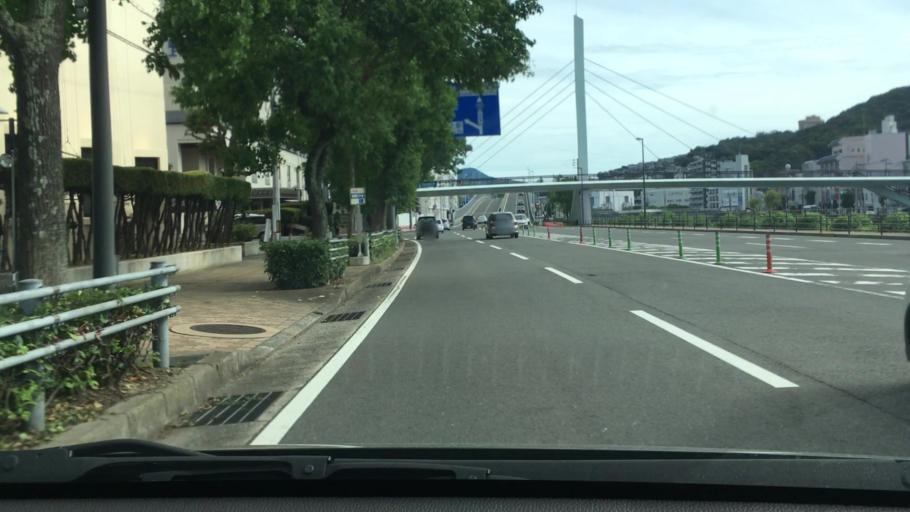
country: JP
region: Nagasaki
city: Nagasaki-shi
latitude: 32.7670
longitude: 129.8623
